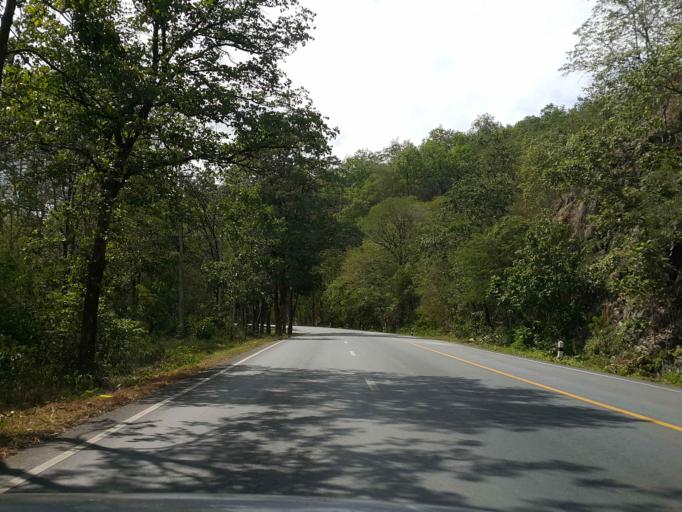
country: TH
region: Tak
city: Tak
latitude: 16.8098
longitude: 98.9830
